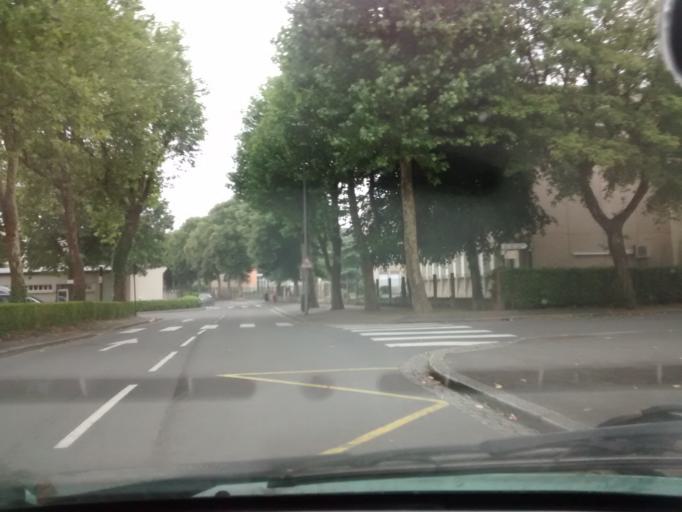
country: FR
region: Lower Normandy
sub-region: Departement de la Manche
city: Agneaux
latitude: 49.1134
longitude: -1.1033
